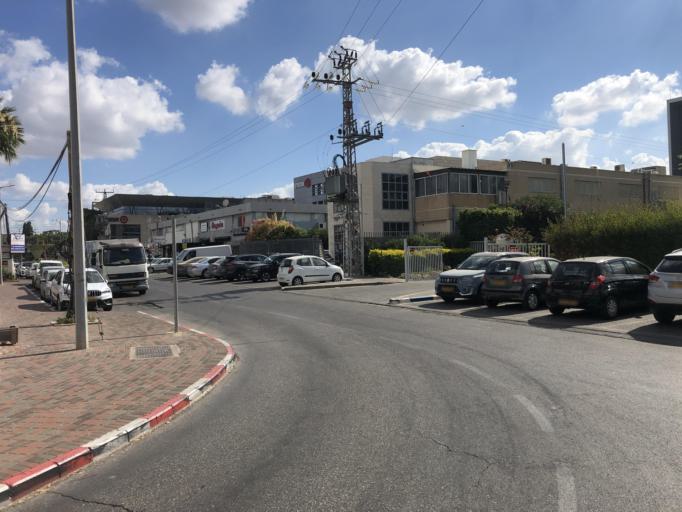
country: IL
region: Central District
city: Yehud
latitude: 32.0269
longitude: 34.8966
